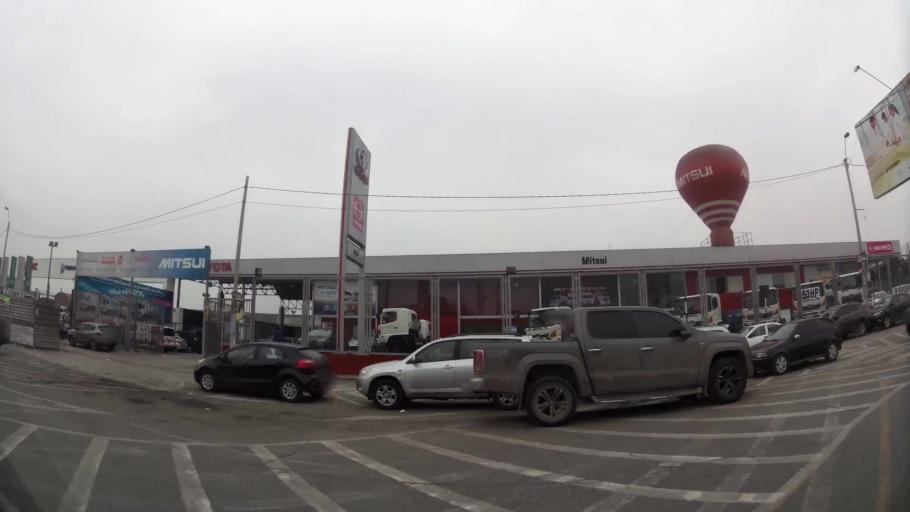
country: PE
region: Lima
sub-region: Lima
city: Vitarte
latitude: -12.0487
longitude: -76.9503
